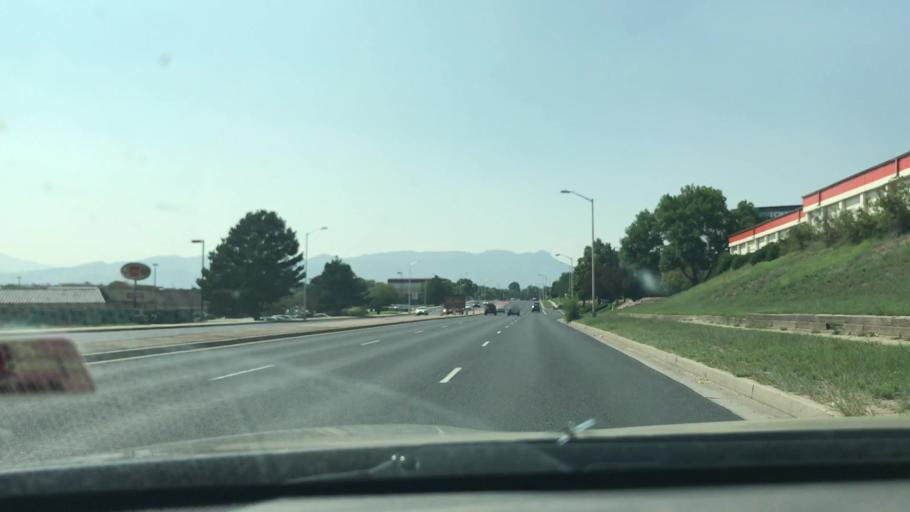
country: US
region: Colorado
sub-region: El Paso County
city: Colorado Springs
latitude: 38.9050
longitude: -104.7766
